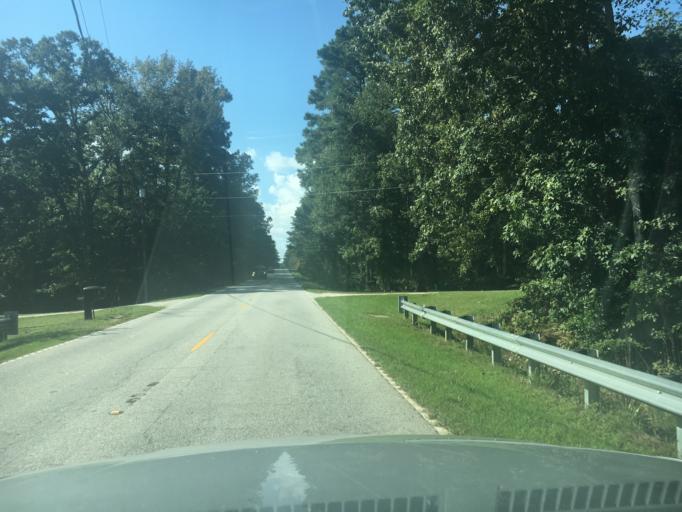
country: US
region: South Carolina
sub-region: Greenwood County
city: Greenwood
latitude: 34.2925
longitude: -82.2120
